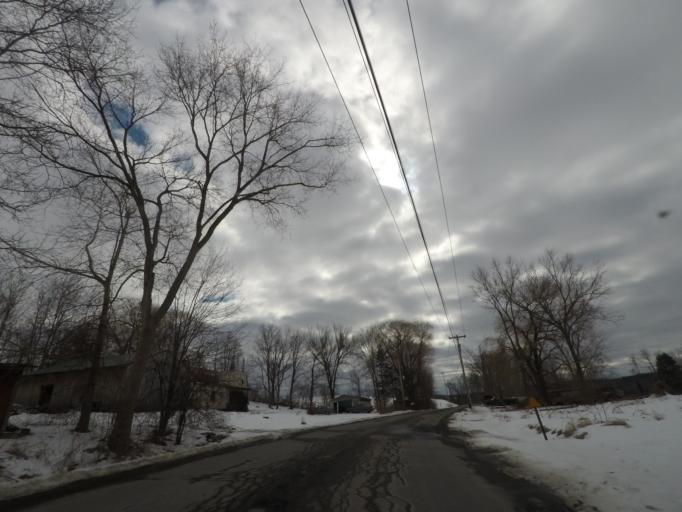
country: US
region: New York
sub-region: Rensselaer County
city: Hoosick Falls
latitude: 42.9243
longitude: -73.4348
